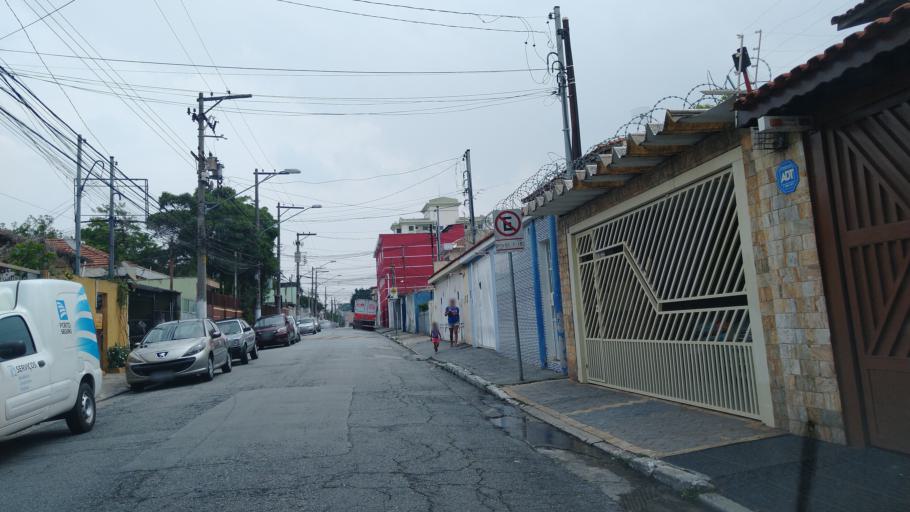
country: BR
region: Sao Paulo
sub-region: Guarulhos
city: Guarulhos
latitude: -23.4891
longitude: -46.5924
